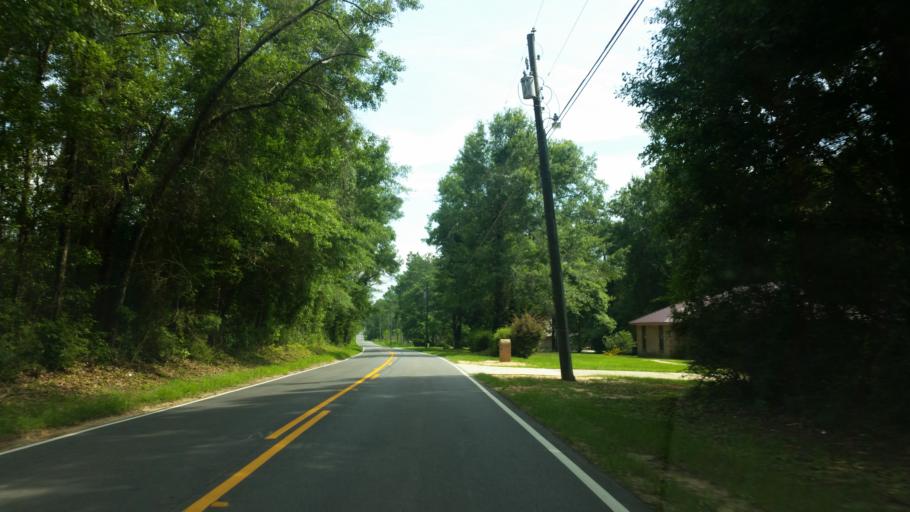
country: US
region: Florida
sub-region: Escambia County
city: Cantonment
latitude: 30.5957
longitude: -87.3954
